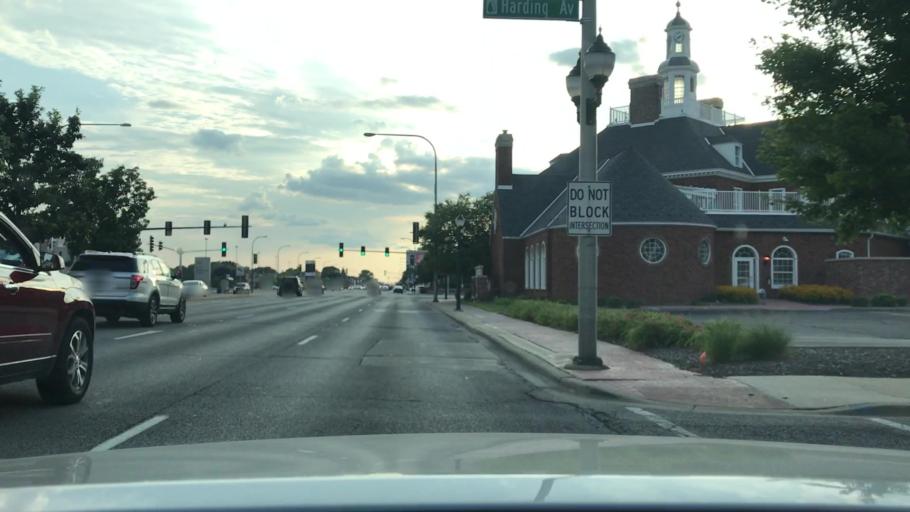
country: US
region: Illinois
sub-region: Cook County
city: Hometown
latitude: 41.7206
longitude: -87.7202
